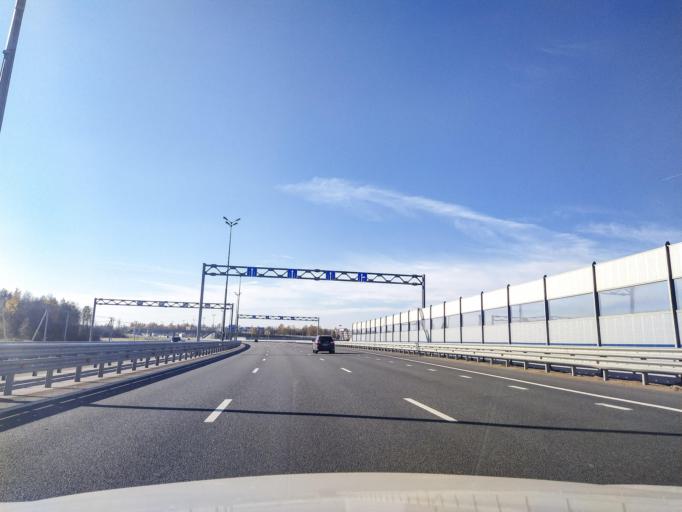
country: RU
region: Leningrad
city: Mariyenburg
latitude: 59.5261
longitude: 30.0843
